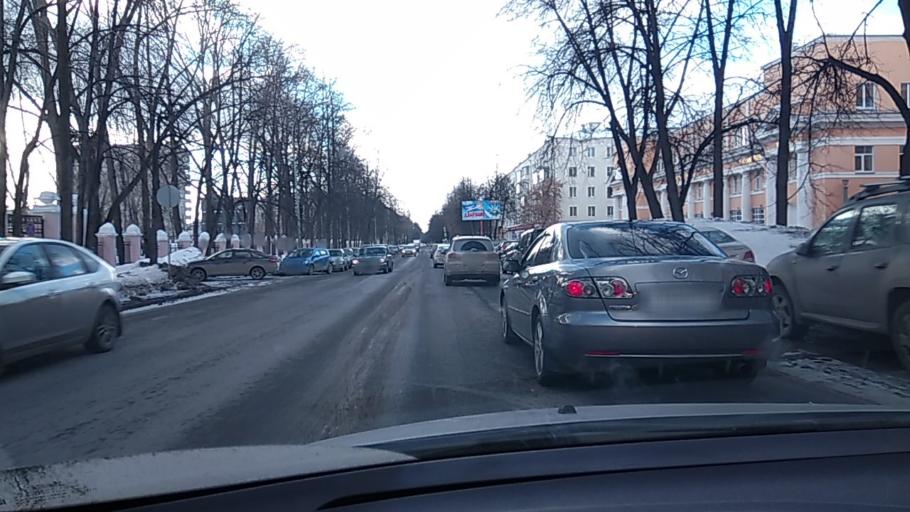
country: RU
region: Sverdlovsk
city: Yekaterinburg
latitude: 56.8460
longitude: 60.6483
